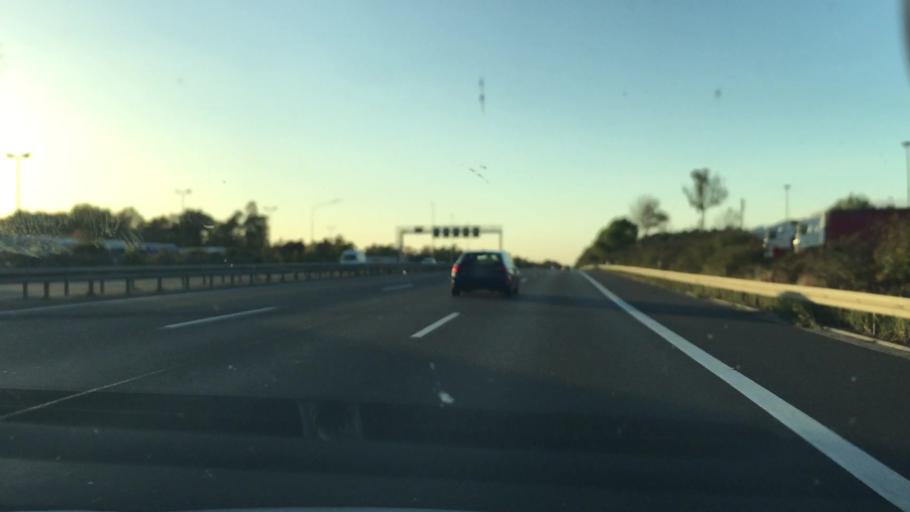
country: DE
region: Saxony-Anhalt
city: Harbke
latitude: 52.2198
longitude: 11.0567
